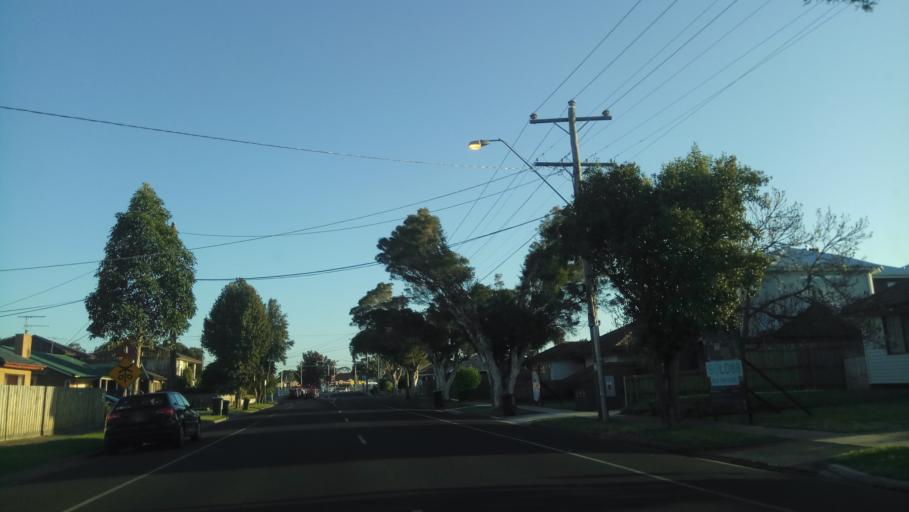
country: AU
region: Victoria
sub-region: Hobsons Bay
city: Altona
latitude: -37.8666
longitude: 144.8125
